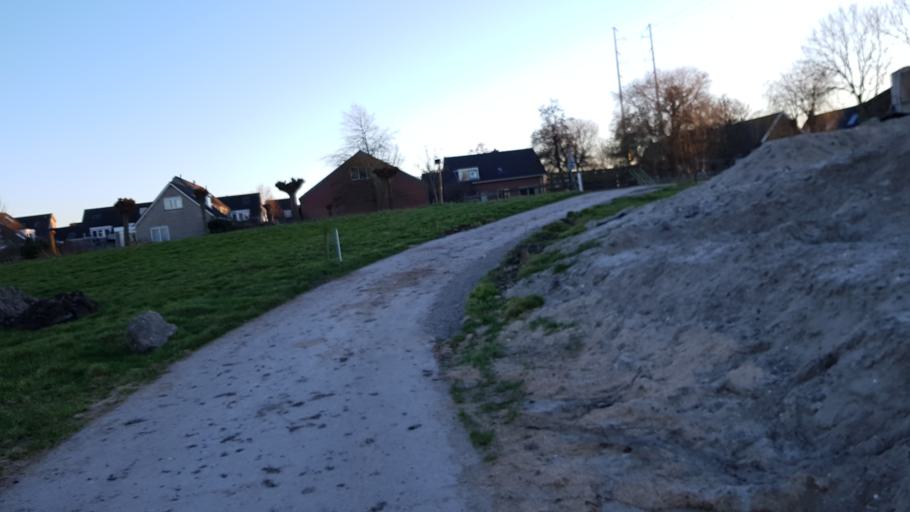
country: NL
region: South Holland
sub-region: Gemeente Rijnwoude
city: Benthuizen
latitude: 52.0982
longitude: 4.5766
